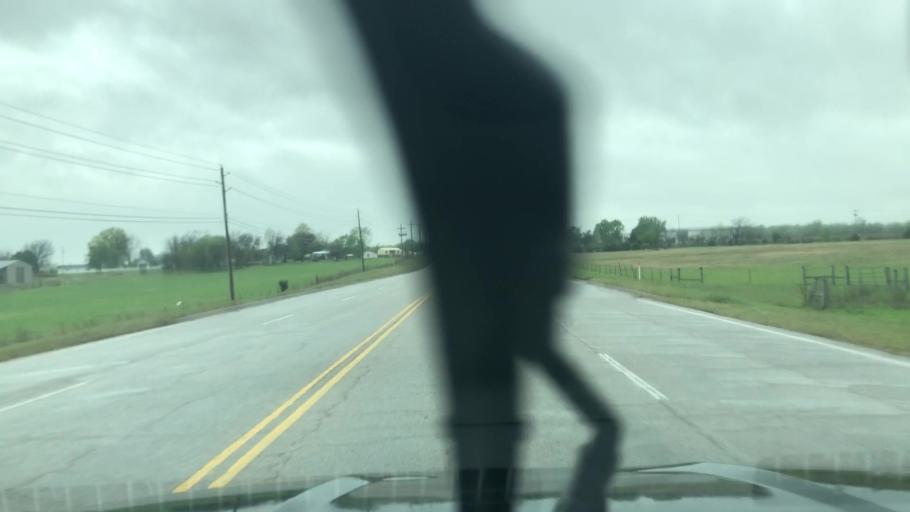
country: US
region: Oklahoma
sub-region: Tulsa County
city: Owasso
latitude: 36.2640
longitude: -95.8806
